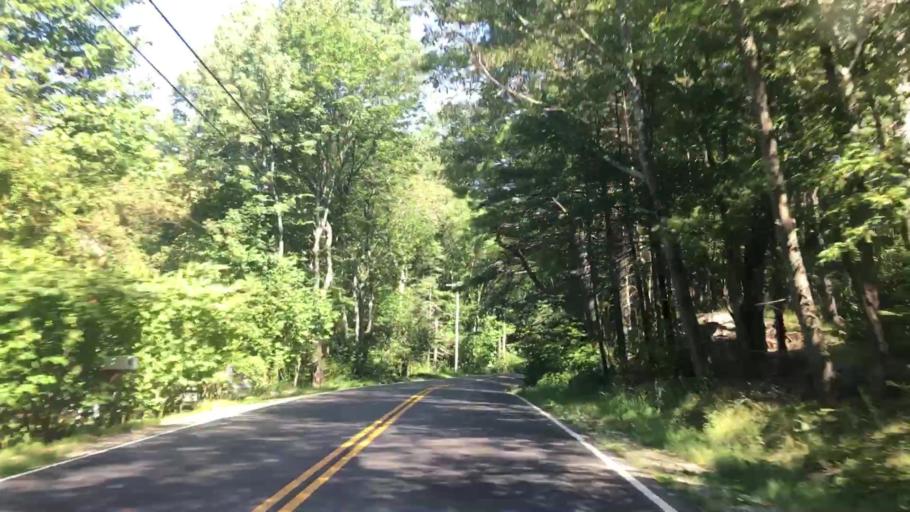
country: US
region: Maine
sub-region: Sagadahoc County
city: Topsham
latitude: 43.9848
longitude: -69.9859
